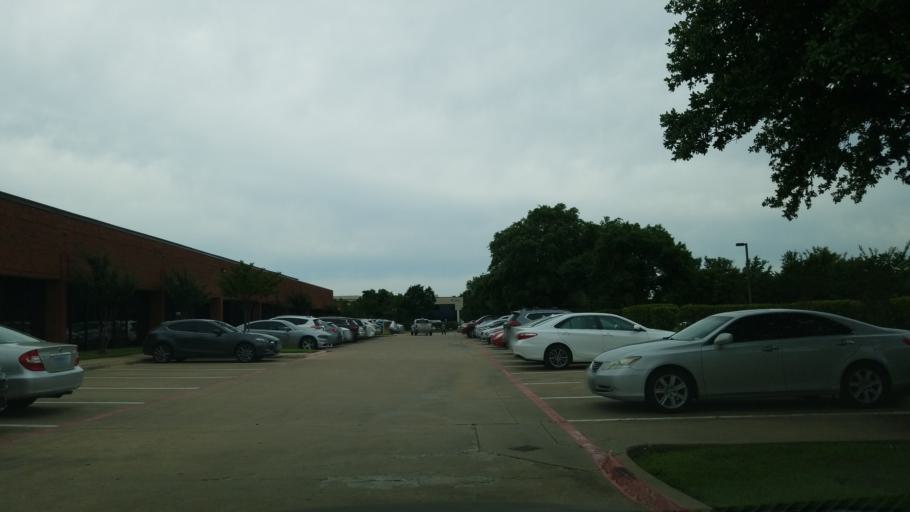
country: US
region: Texas
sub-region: Dallas County
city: Coppell
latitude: 32.8955
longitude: -96.9890
